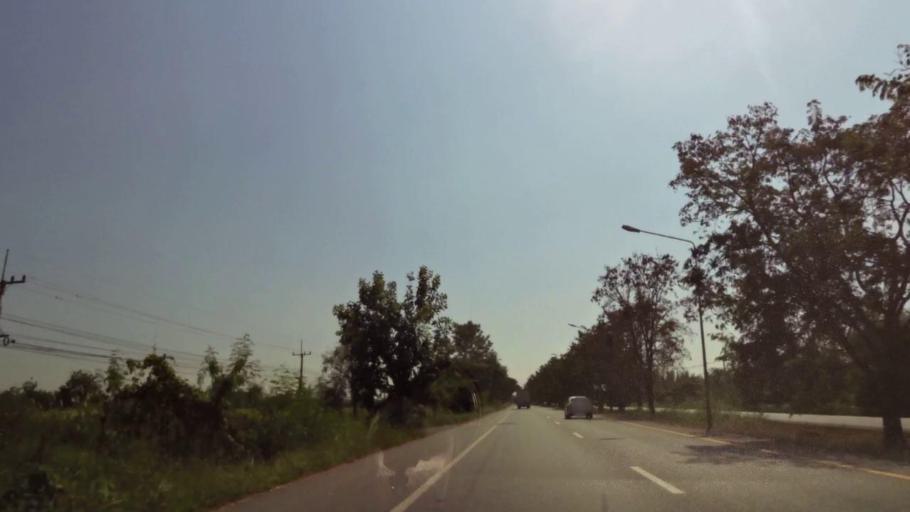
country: TH
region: Nakhon Sawan
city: Kao Liao
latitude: 15.9096
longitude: 100.1124
